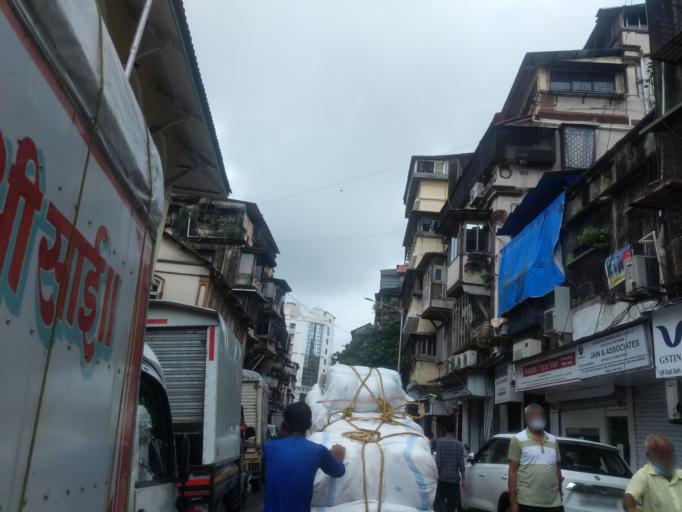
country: IN
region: Maharashtra
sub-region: Raigarh
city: Uran
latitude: 18.9504
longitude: 72.8268
